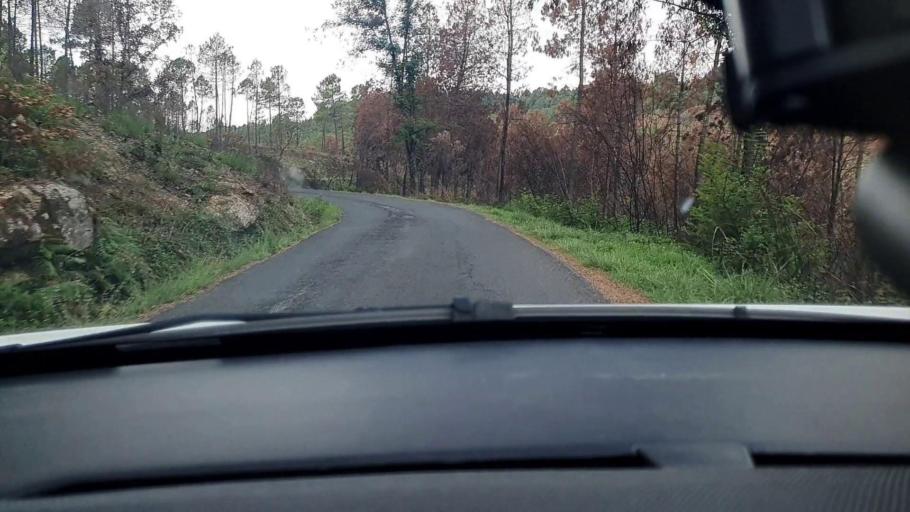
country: FR
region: Languedoc-Roussillon
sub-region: Departement du Gard
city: Besseges
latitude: 44.3216
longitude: 4.0856
